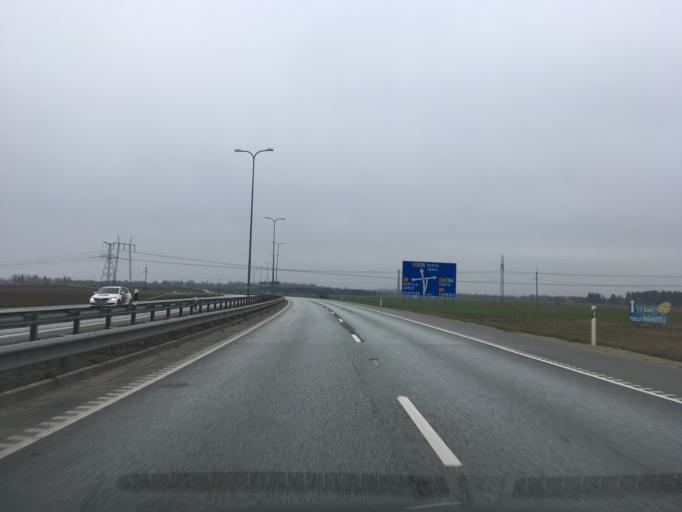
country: EE
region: Ida-Virumaa
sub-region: Kohtla-Jaerve linn
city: Kohtla-Jarve
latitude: 59.3920
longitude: 27.3375
